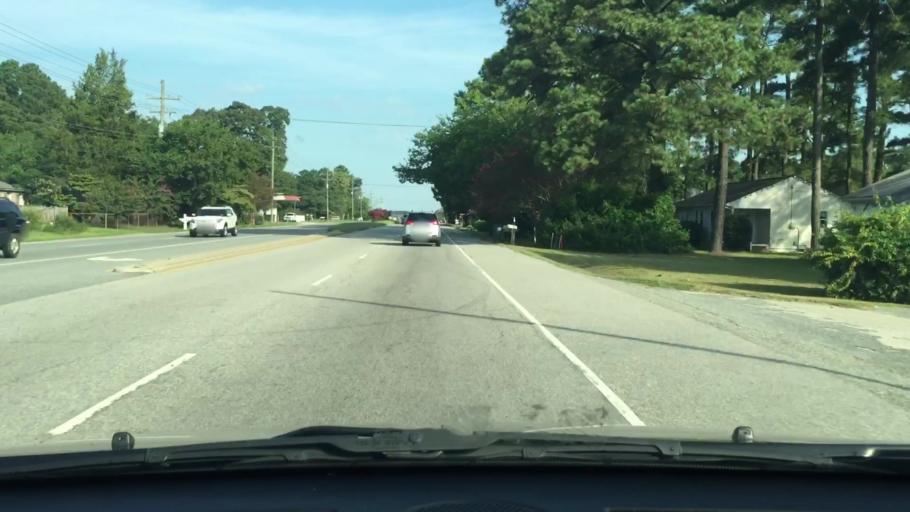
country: US
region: Virginia
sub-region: Isle of Wight County
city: Carrollton
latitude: 36.9425
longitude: -76.5897
